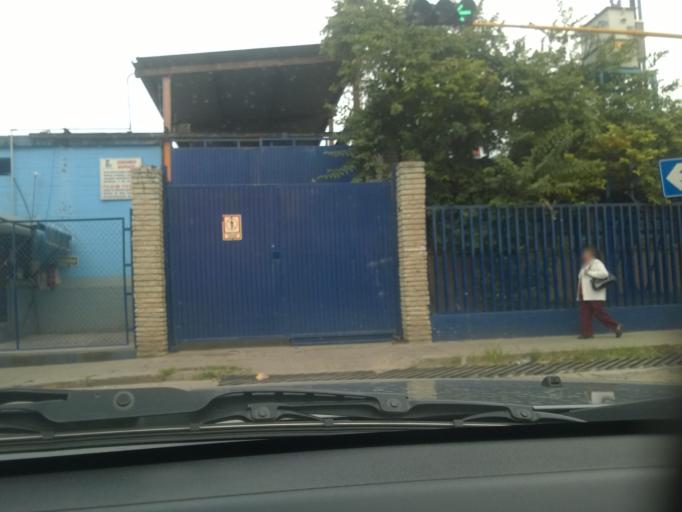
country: MX
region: Guanajuato
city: Leon
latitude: 21.1310
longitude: -101.6908
